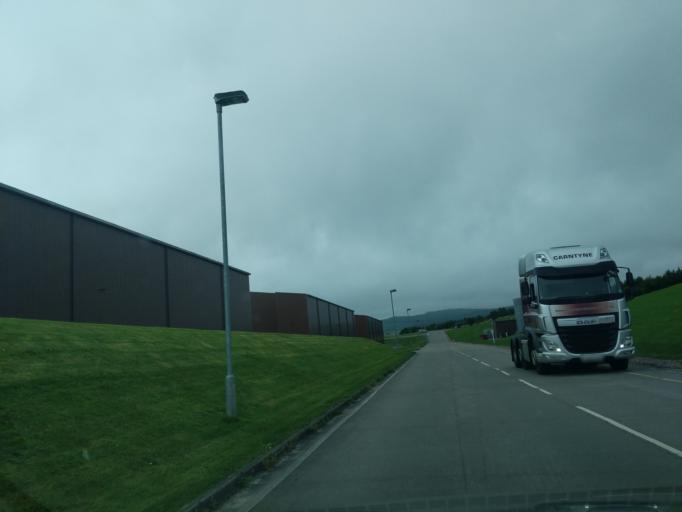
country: GB
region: Scotland
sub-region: Moray
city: Rothes
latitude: 57.4898
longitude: -3.2085
